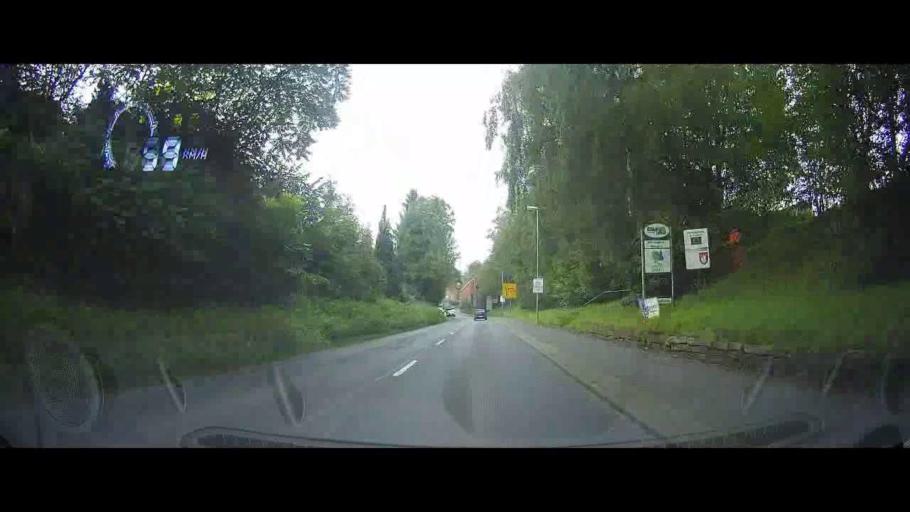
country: DE
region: Lower Saxony
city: Uslar
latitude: 51.6555
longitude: 9.6458
